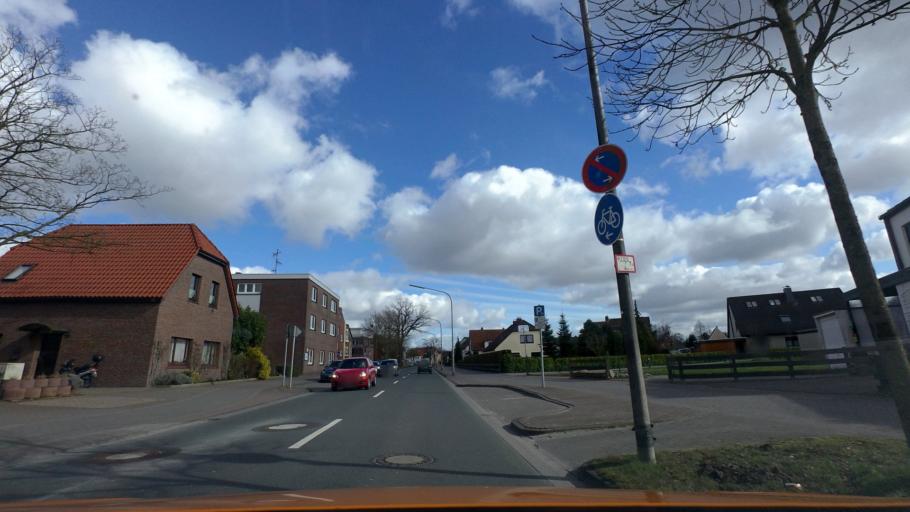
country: DE
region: Lower Saxony
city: Oldenburg
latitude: 53.1409
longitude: 8.1793
